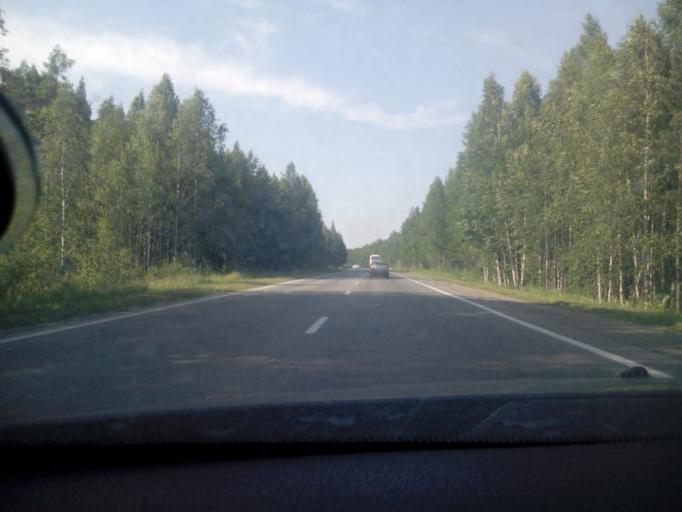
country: RU
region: Sverdlovsk
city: Verkh-Neyvinskiy
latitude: 57.2816
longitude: 60.2967
